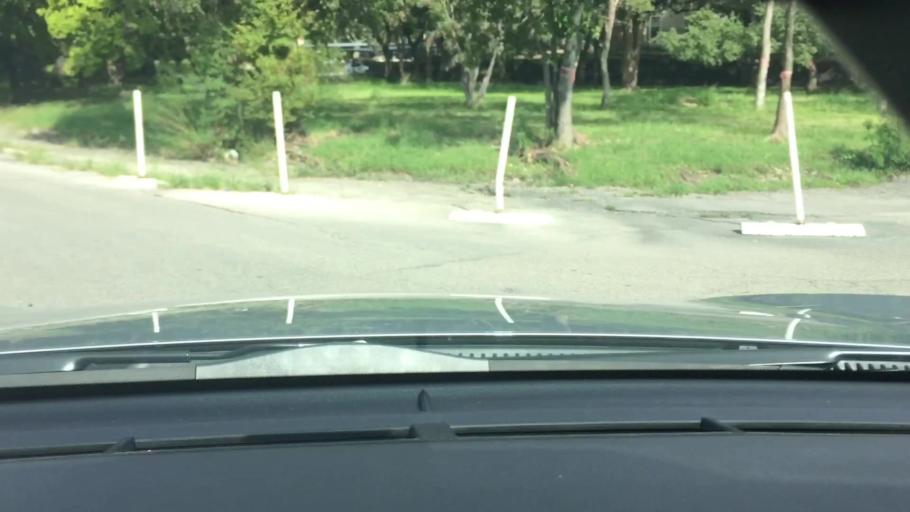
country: US
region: Texas
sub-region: Bexar County
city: Shavano Park
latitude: 29.5491
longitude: -98.5671
